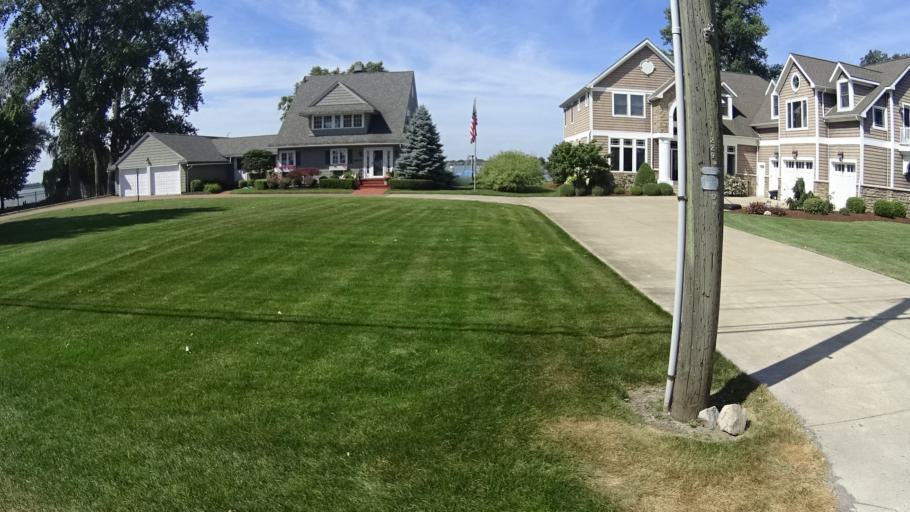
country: US
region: Ohio
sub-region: Erie County
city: Sandusky
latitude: 41.4555
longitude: -82.6522
